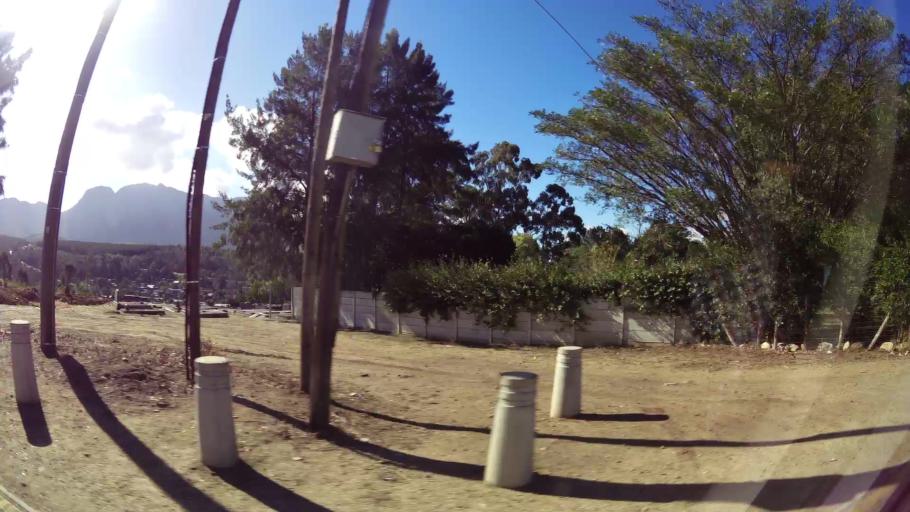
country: ZA
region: Western Cape
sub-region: Eden District Municipality
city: George
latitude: -33.9403
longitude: 22.4056
